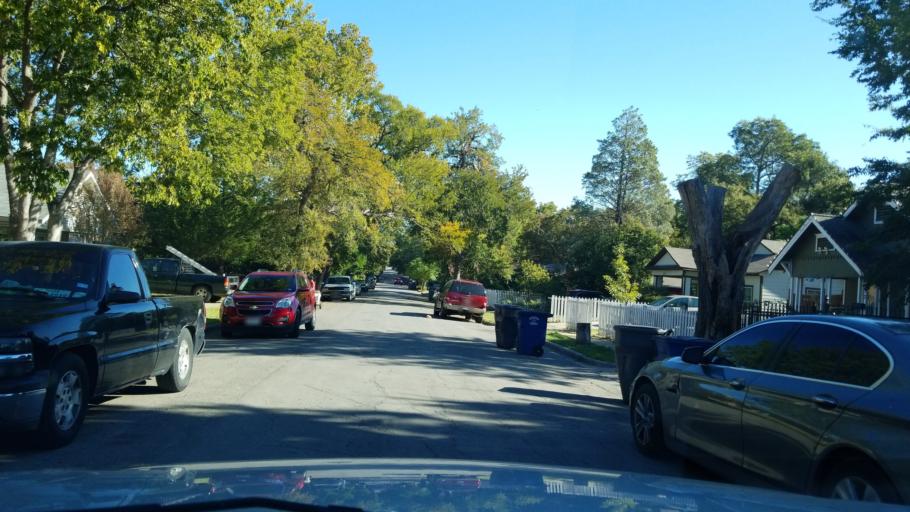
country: US
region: Texas
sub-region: Dallas County
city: Highland Park
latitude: 32.8012
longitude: -96.7513
